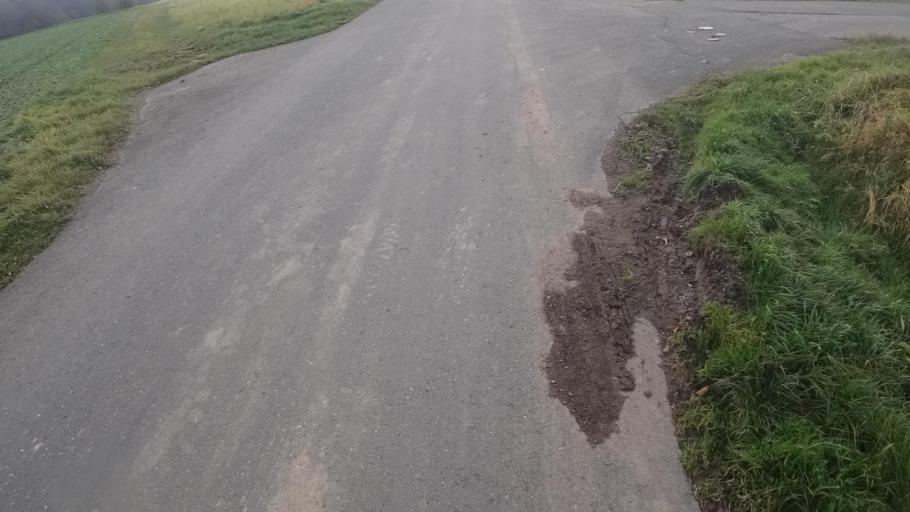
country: DE
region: Rheinland-Pfalz
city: Bickenbach
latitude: 50.1220
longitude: 7.5328
